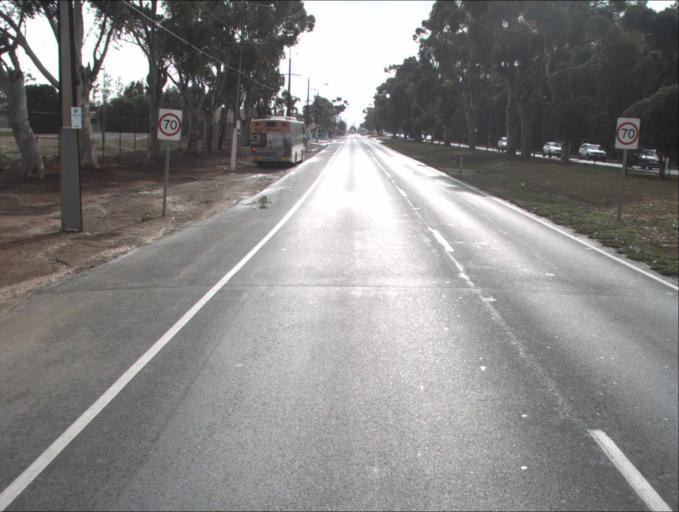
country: AU
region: South Australia
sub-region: Port Adelaide Enfield
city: Enfield
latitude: -34.8435
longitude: 138.6035
